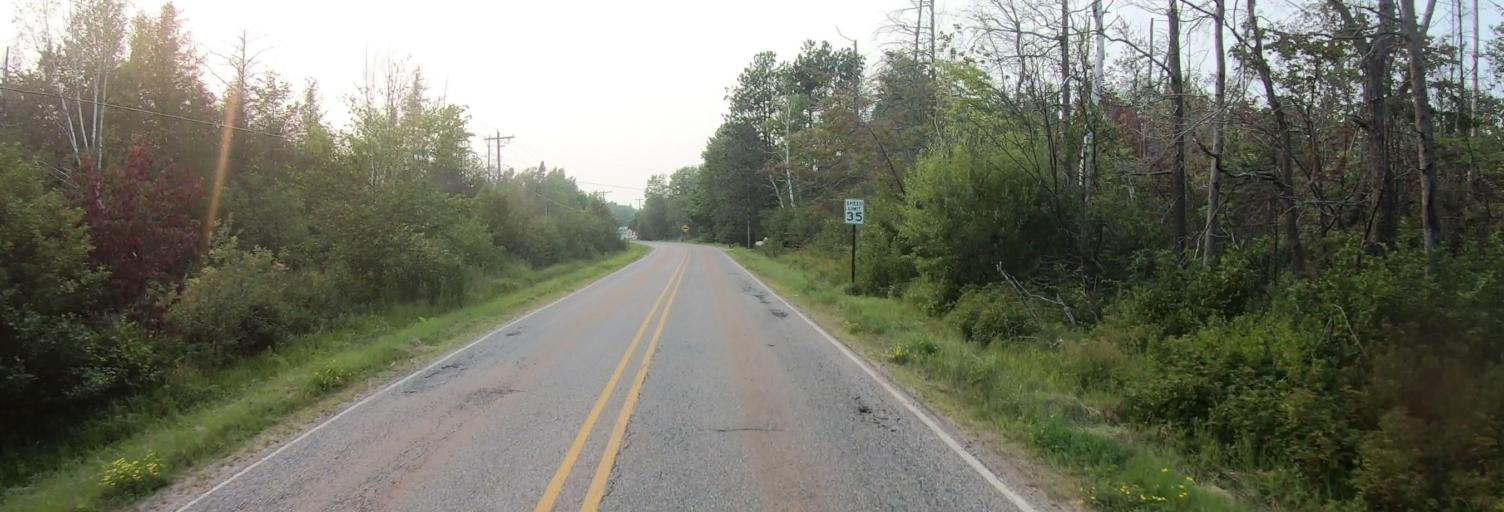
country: US
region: Michigan
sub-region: Chippewa County
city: Sault Ste. Marie
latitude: 46.4845
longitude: -84.6682
